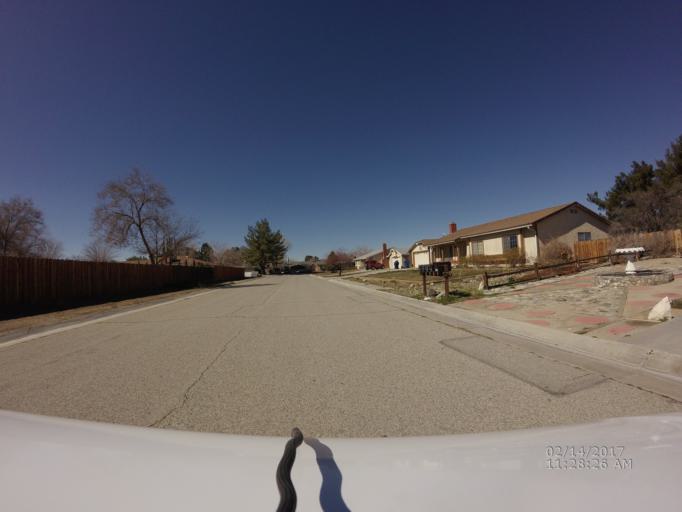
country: US
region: California
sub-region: Los Angeles County
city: Littlerock
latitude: 34.5592
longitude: -117.9573
